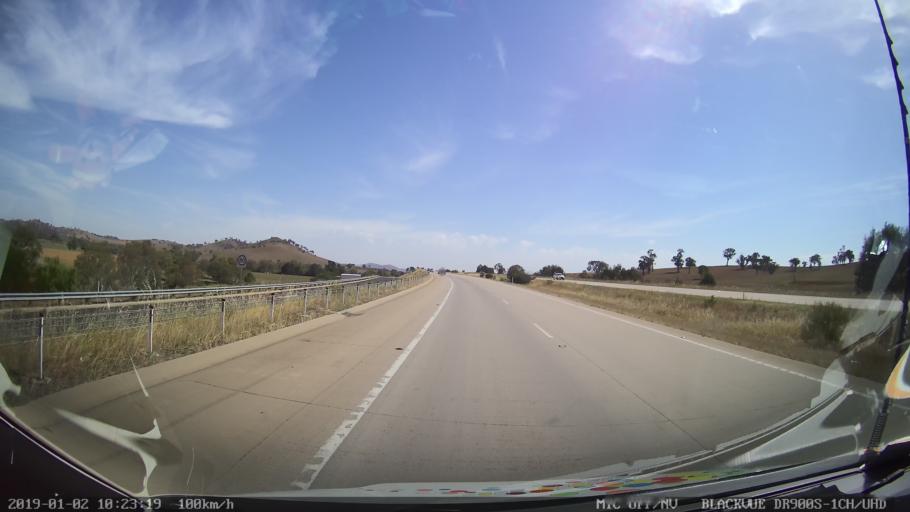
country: AU
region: New South Wales
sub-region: Gundagai
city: Gundagai
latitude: -34.9607
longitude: 148.1563
